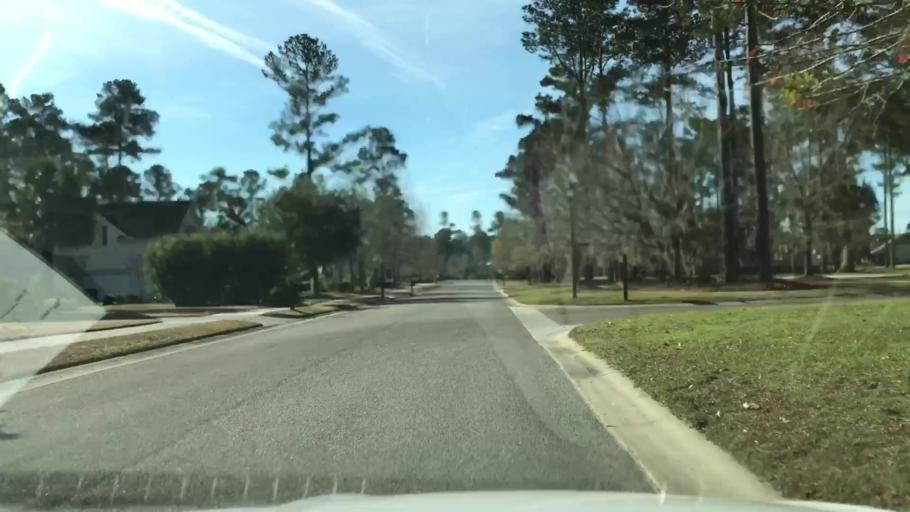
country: US
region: South Carolina
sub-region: Beaufort County
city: Bluffton
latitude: 32.2429
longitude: -80.9137
